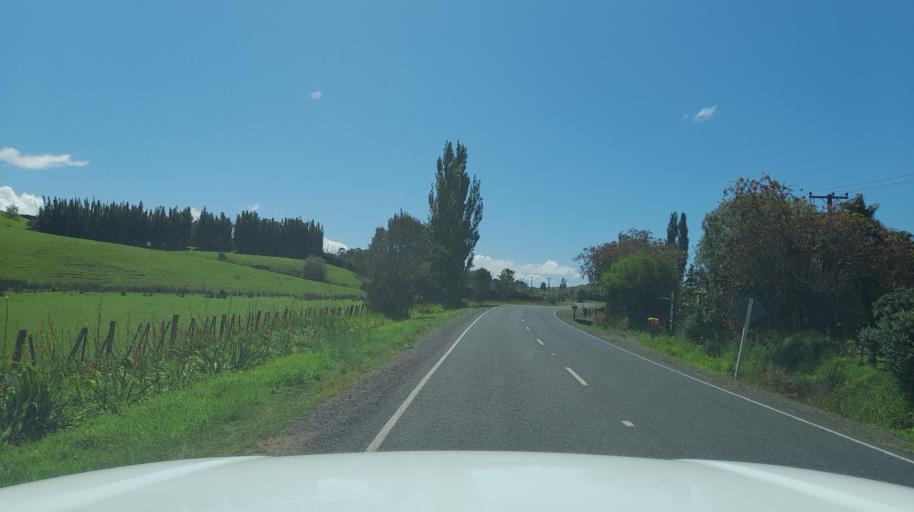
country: NZ
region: Northland
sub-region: Far North District
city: Taipa
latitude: -35.0785
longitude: 173.5093
